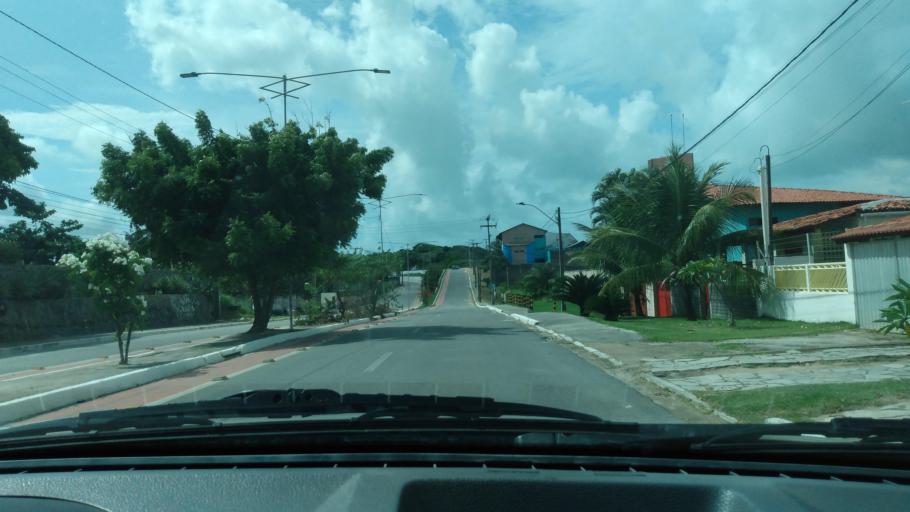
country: BR
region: Pernambuco
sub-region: Cabo De Santo Agostinho
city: Cabo
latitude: -8.3097
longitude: -34.9474
